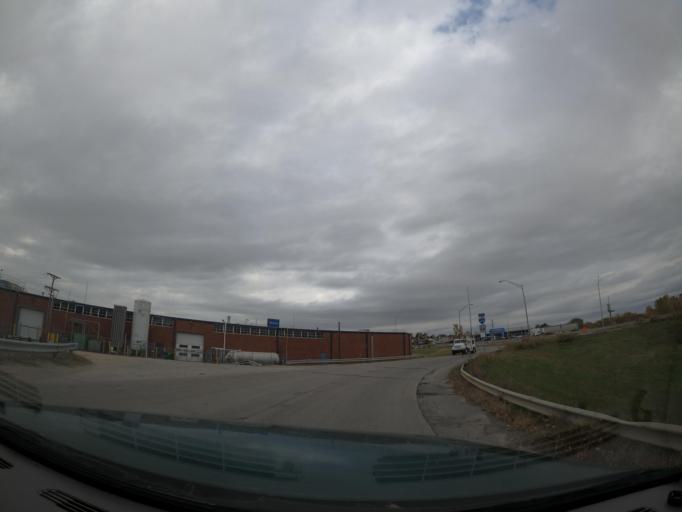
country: US
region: Oklahoma
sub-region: Tulsa County
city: Tulsa
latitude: 36.0889
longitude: -95.9957
